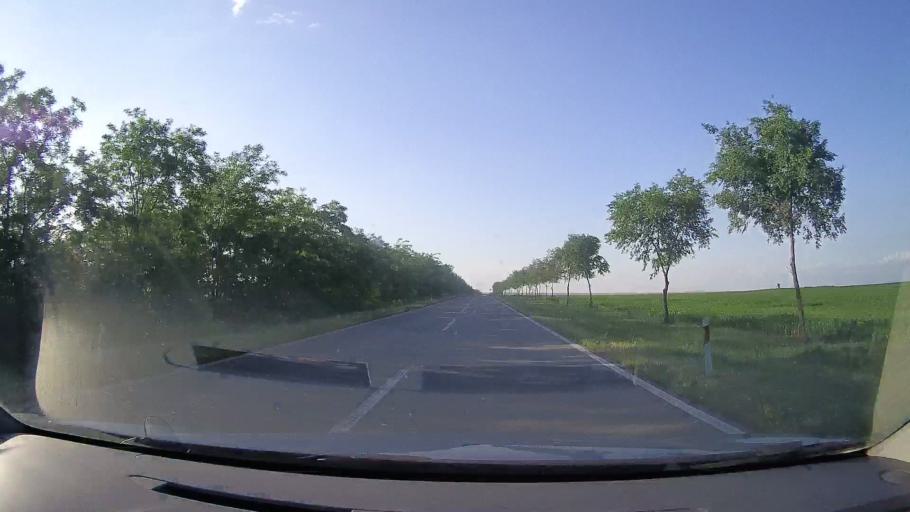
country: RO
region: Timis
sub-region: Comuna Moravita
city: Moravita
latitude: 45.2048
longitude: 21.2998
